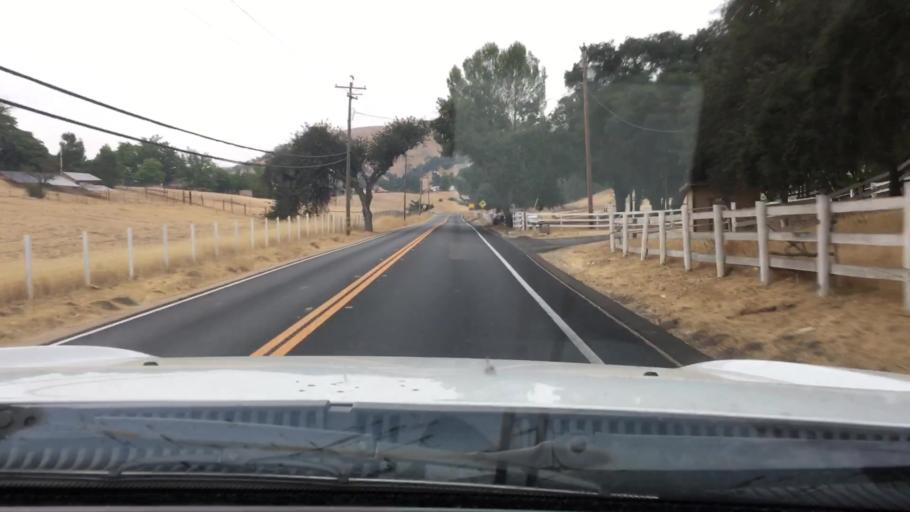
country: US
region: California
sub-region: San Luis Obispo County
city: Atascadero
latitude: 35.5068
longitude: -120.6443
